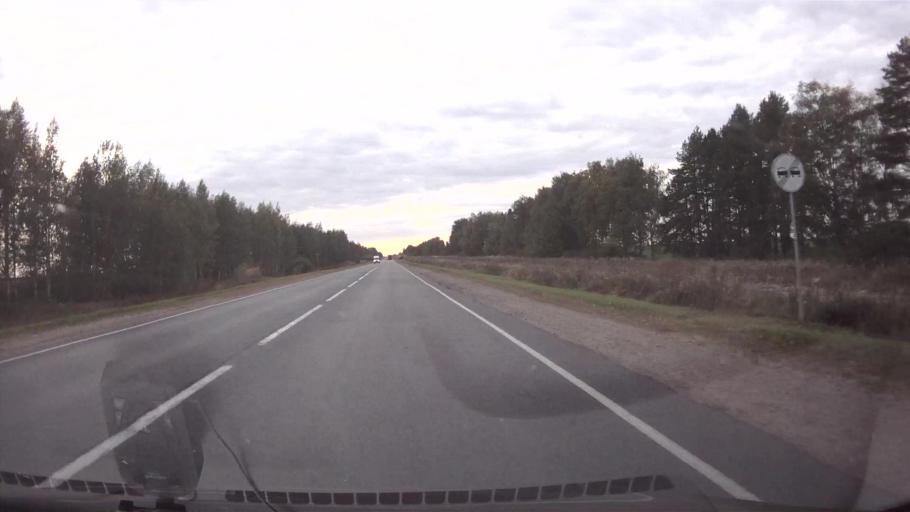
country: RU
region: Mariy-El
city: Sovetskiy
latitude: 56.7474
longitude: 48.3152
